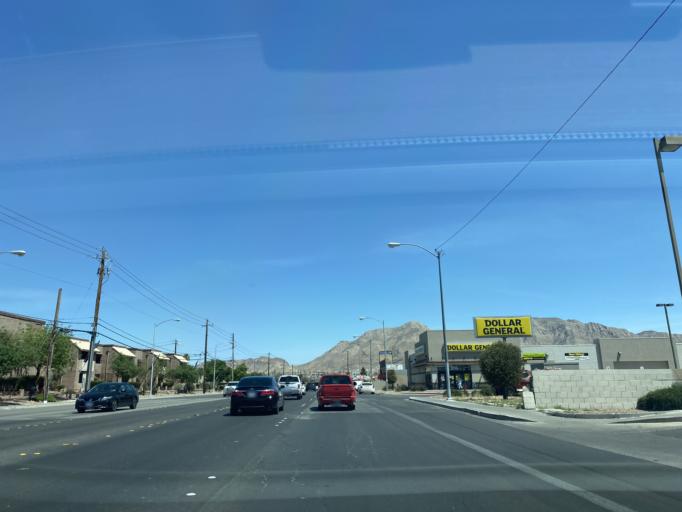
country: US
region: Nevada
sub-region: Clark County
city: Sunrise Manor
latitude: 36.1962
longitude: -115.0615
